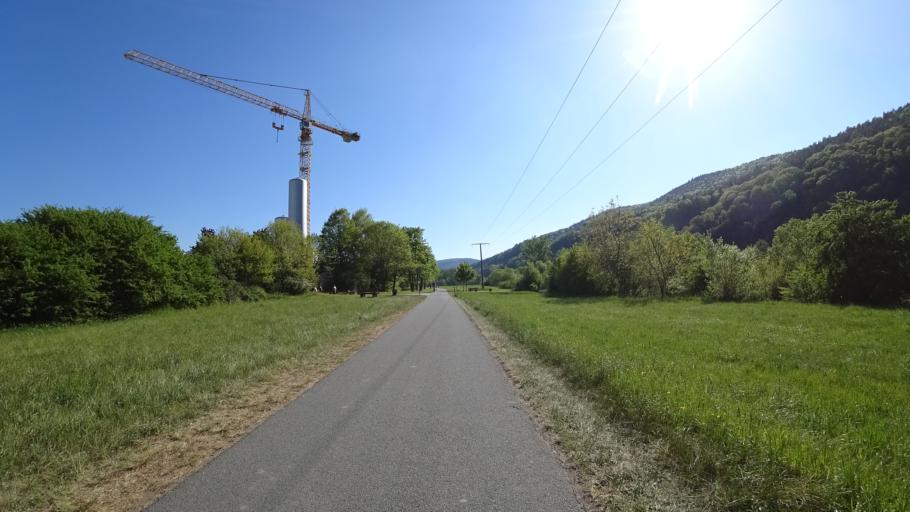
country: DE
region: Bavaria
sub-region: Regierungsbezirk Unterfranken
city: Burgstadt
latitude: 49.7319
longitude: 9.2719
